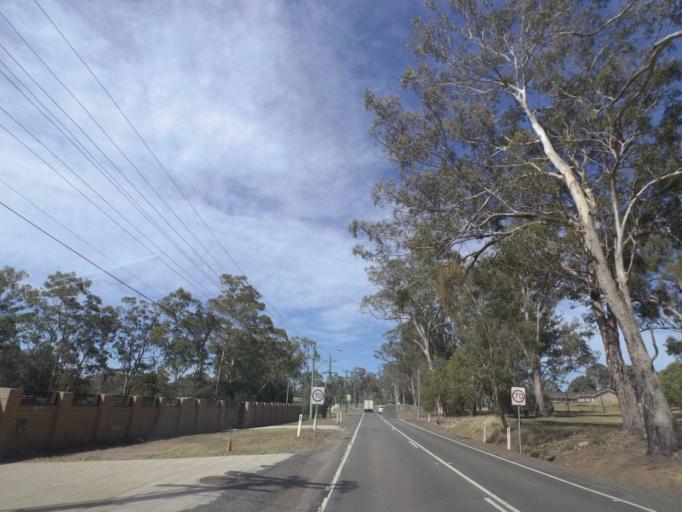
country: AU
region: New South Wales
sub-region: Campbelltown Municipality
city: Denham Court
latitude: -33.9834
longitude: 150.8454
